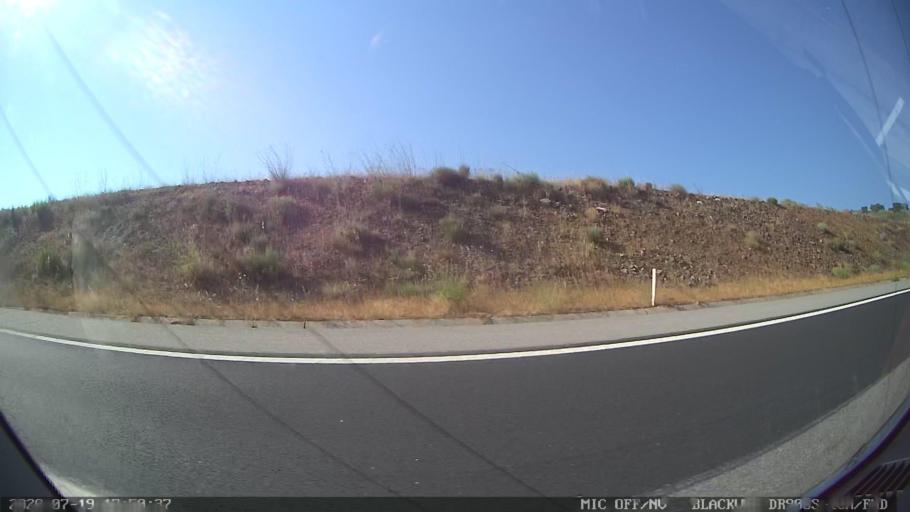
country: PT
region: Braganca
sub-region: Macedo de Cavaleiros
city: Macedo de Cavaleiros
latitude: 41.5666
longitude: -7.0060
